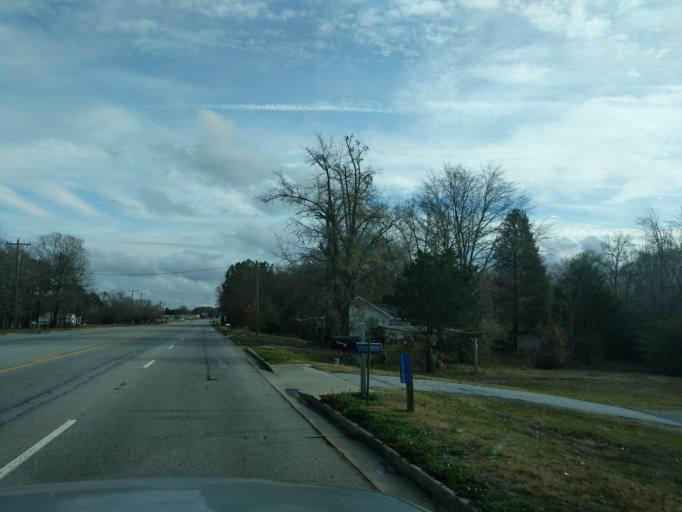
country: US
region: South Carolina
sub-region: Anderson County
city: Honea Path
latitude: 34.5046
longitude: -82.2949
